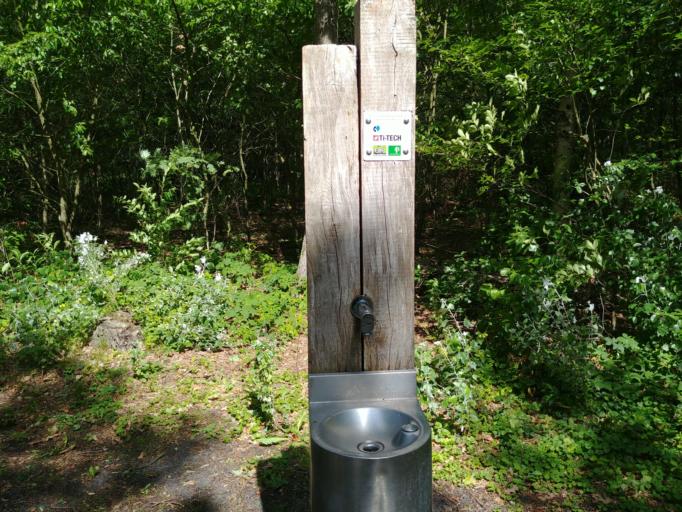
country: NL
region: North Holland
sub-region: Gemeente Bergen
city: Egmond aan Zee
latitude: 52.6814
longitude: 4.6717
